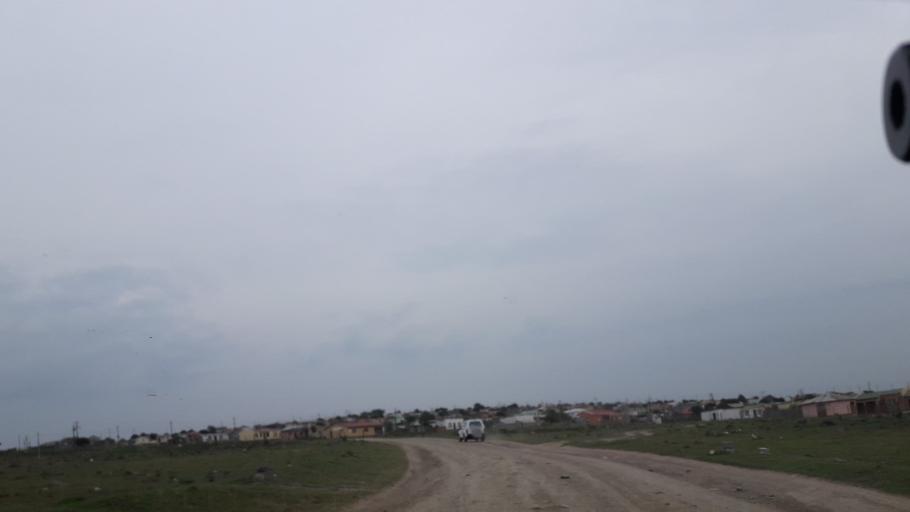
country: ZA
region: Eastern Cape
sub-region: Buffalo City Metropolitan Municipality
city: Bhisho
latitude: -32.8329
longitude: 27.3741
